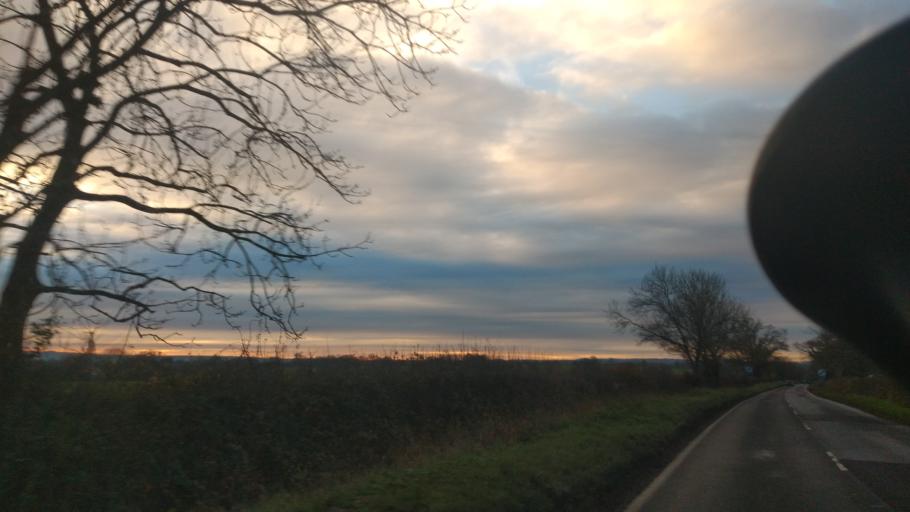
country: GB
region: England
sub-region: Wiltshire
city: Wingfield
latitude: 51.3082
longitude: -2.2570
